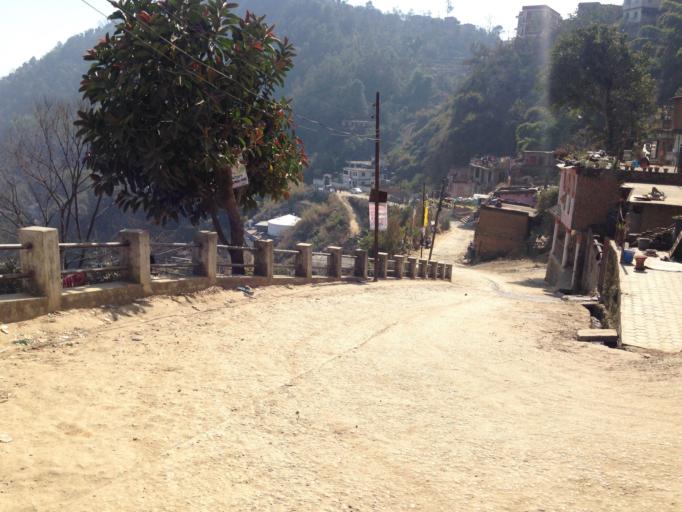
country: NP
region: Central Region
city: Kirtipur
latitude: 27.7241
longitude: 85.2749
